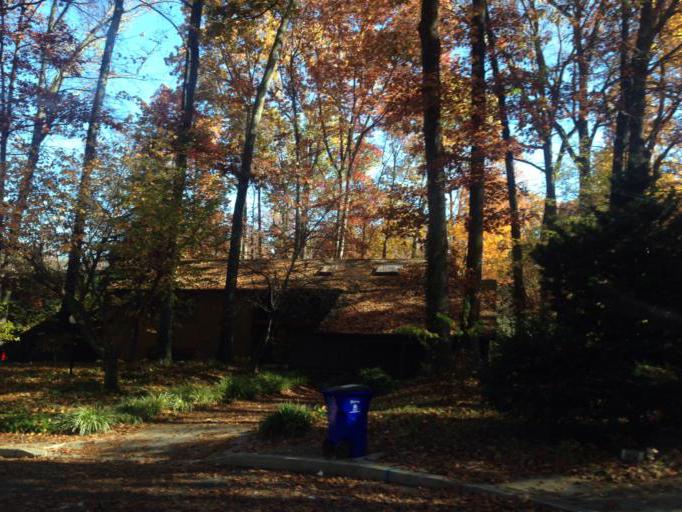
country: US
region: Maryland
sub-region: Howard County
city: Riverside
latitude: 39.1941
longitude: -76.8785
